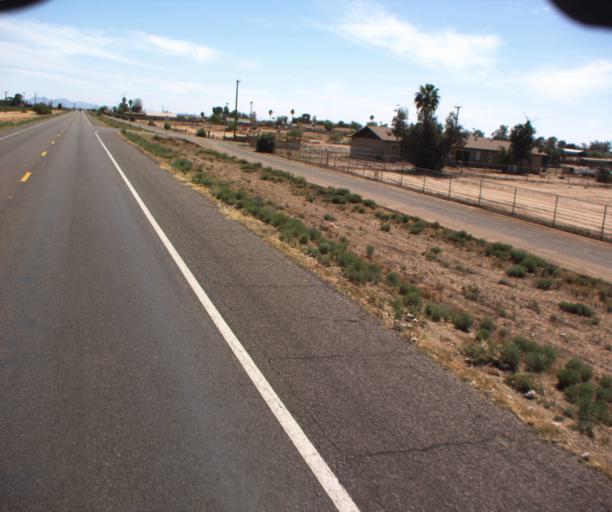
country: US
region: Arizona
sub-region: Pinal County
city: Eloy
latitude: 32.7888
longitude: -111.5155
